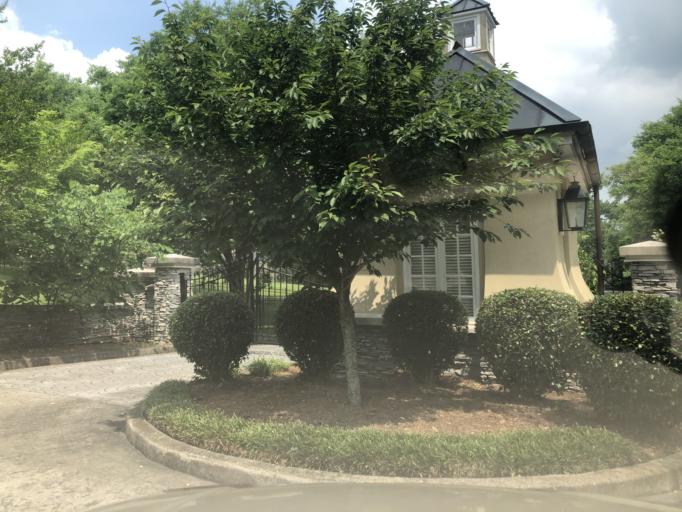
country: US
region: Tennessee
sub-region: Davidson County
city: Lakewood
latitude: 36.2389
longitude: -86.6112
